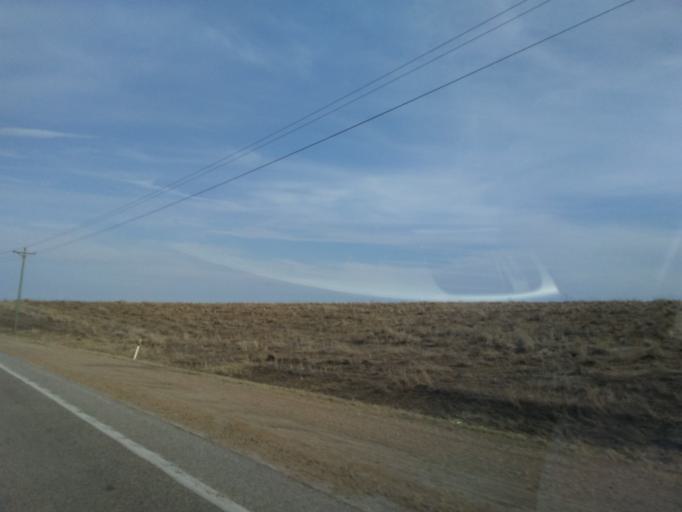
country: US
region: Wisconsin
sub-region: Grant County
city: Fennimore
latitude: 42.9737
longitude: -90.7471
